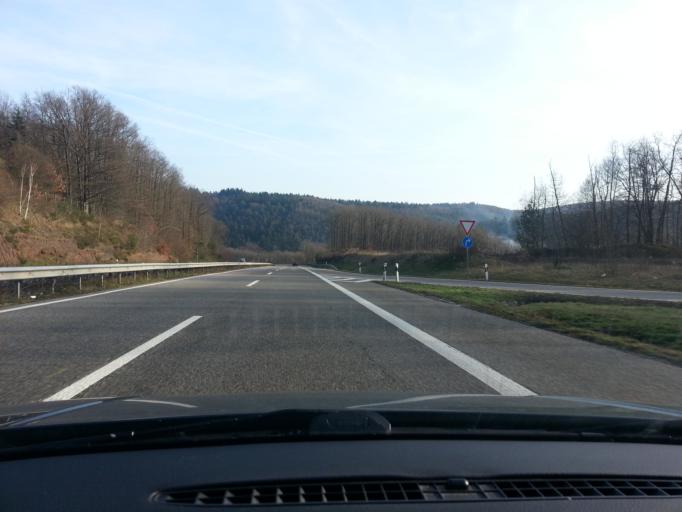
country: DE
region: Rheinland-Pfalz
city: Pirmasens
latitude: 49.2070
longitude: 7.6263
